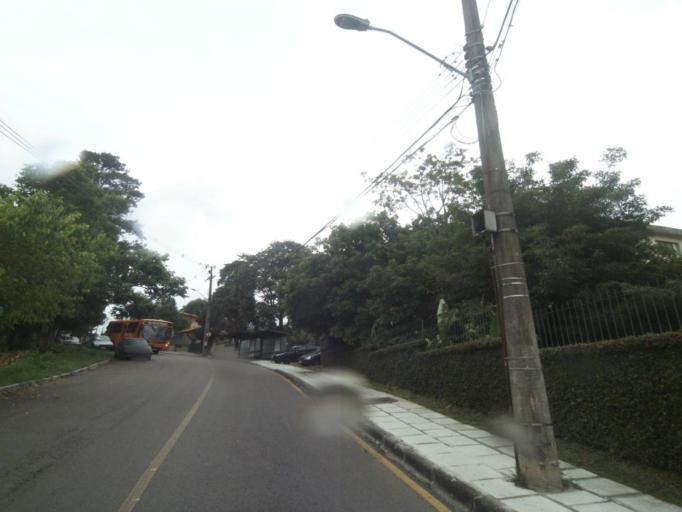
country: BR
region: Parana
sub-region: Curitiba
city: Curitiba
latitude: -25.4621
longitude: -49.3327
